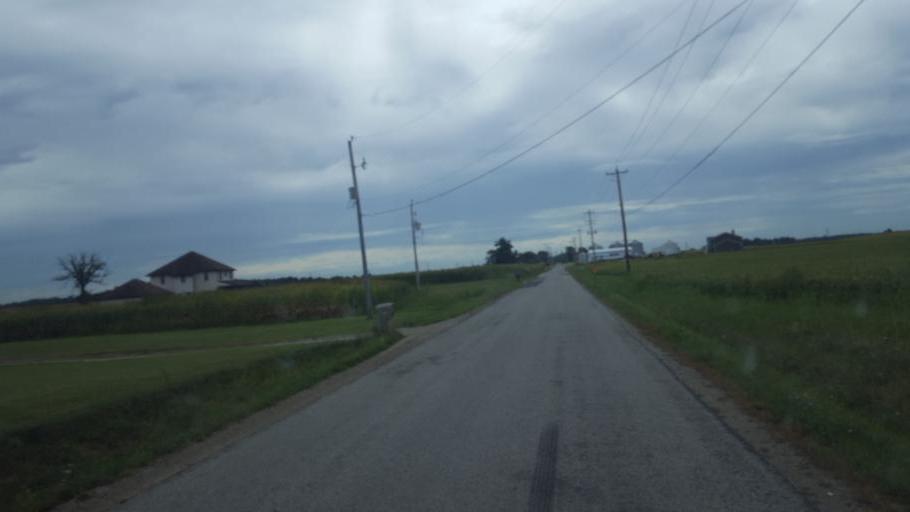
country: US
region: Ohio
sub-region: Knox County
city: Centerburg
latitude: 40.2827
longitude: -82.7225
